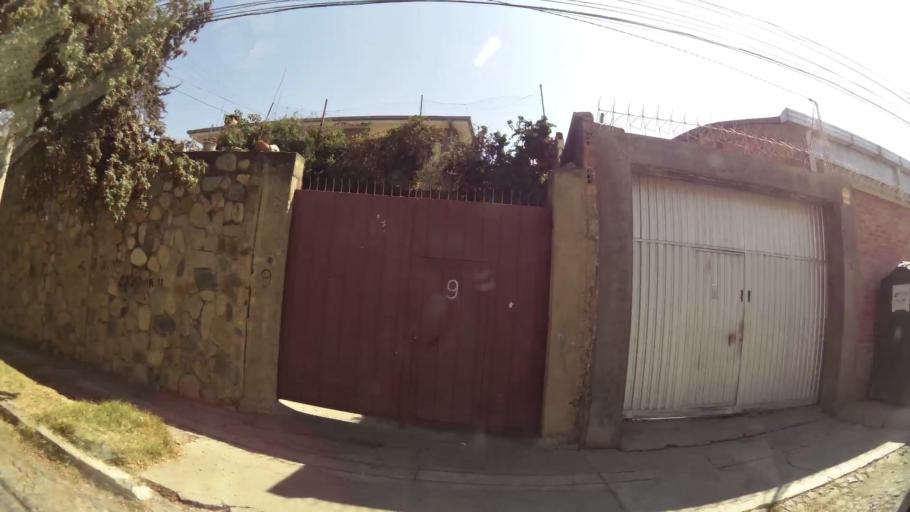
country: BO
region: La Paz
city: La Paz
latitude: -16.5419
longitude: -68.0684
